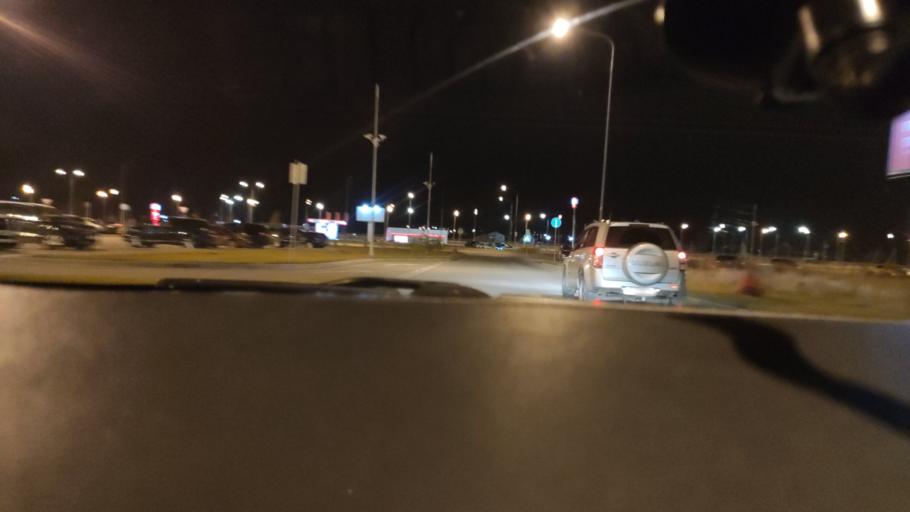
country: RU
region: Perm
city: Kultayevo
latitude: 57.9178
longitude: 56.0099
